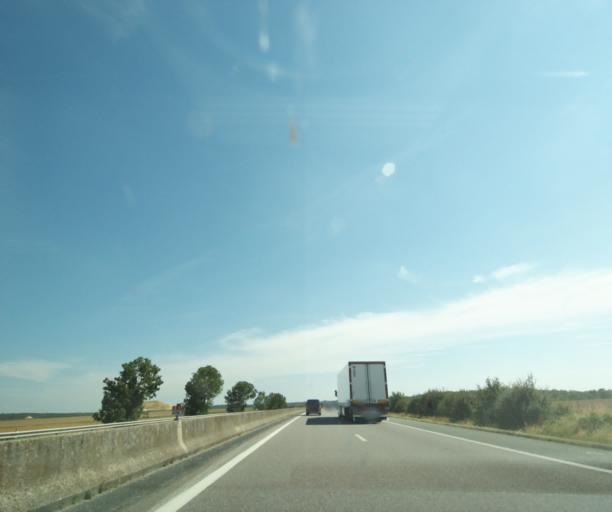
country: FR
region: Lorraine
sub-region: Departement de Meurthe-et-Moselle
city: Colombey-les-Belles
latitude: 48.4721
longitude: 5.8807
